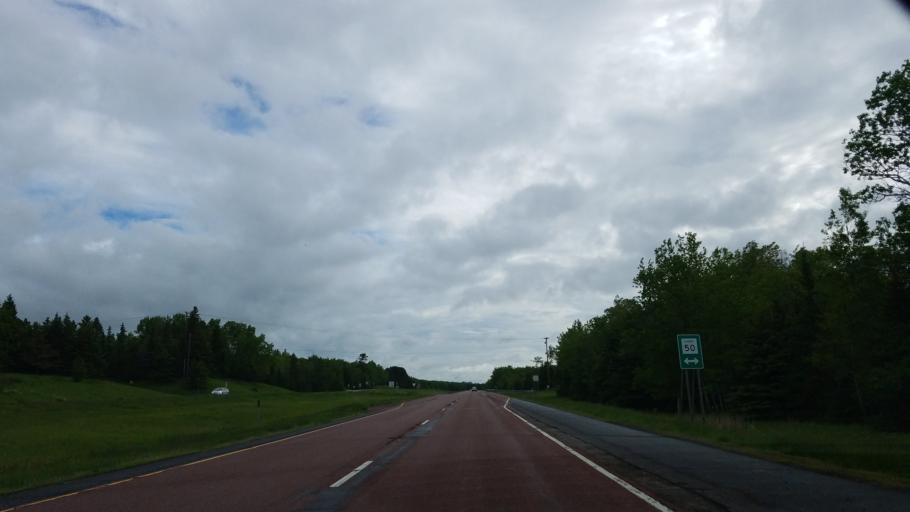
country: US
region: Minnesota
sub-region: Saint Louis County
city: Arnold
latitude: 46.8990
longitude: -91.9023
